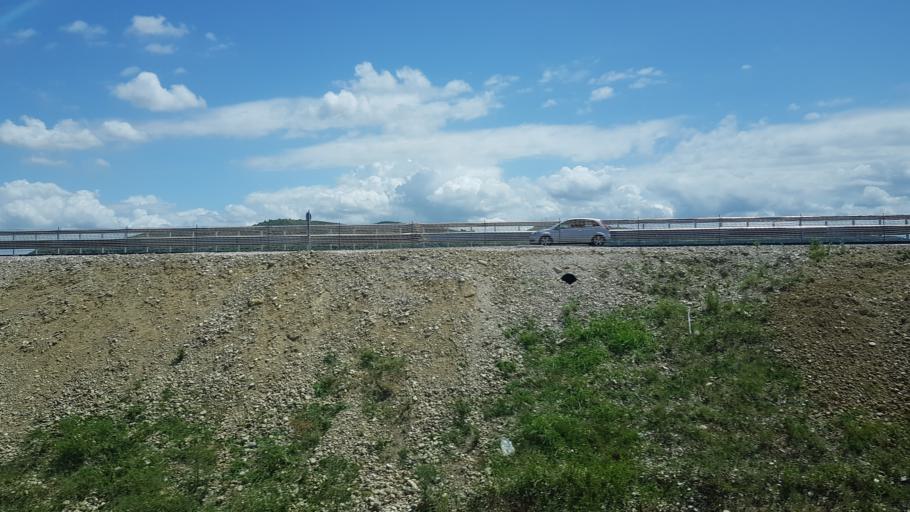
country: AL
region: Fier
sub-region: Rrethi i Fierit
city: Levan
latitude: 40.6718
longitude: 19.4788
